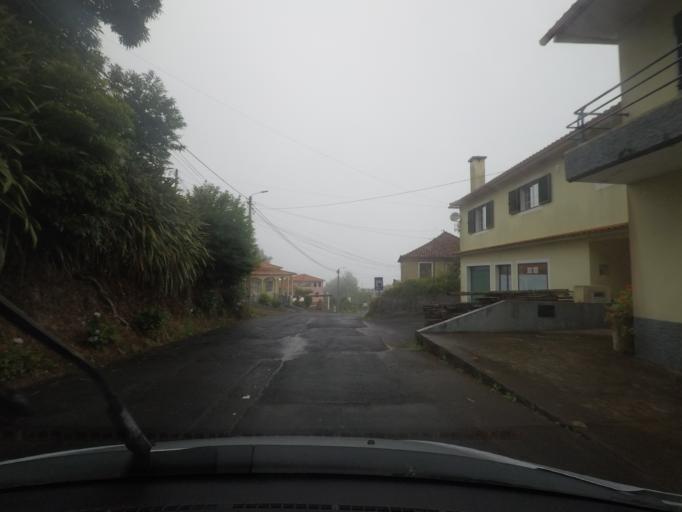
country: PT
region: Madeira
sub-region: Santana
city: Santana
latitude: 32.7996
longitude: -16.8774
